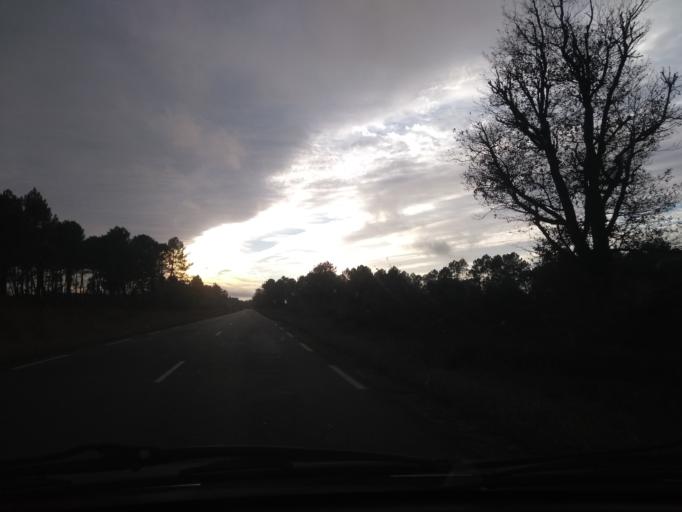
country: FR
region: Aquitaine
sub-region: Departement de la Gironde
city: Le Barp
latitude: 44.5999
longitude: -0.7071
